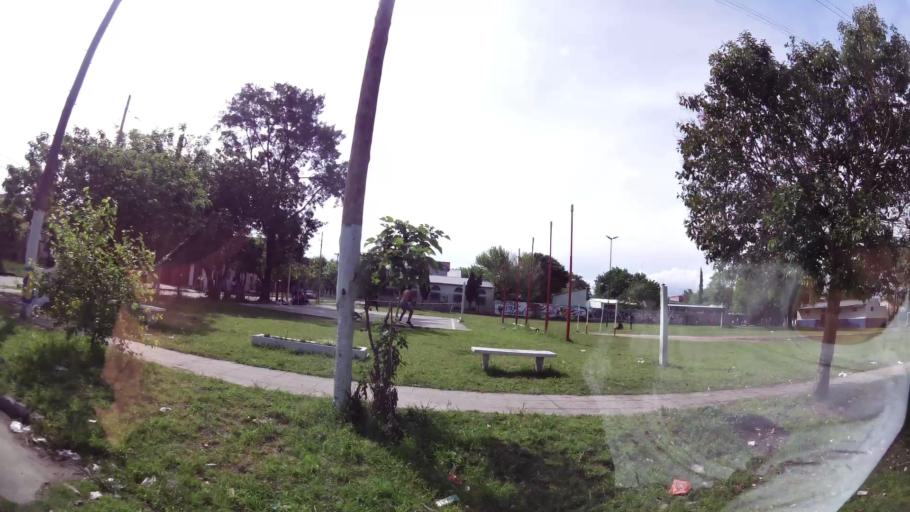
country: AR
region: Buenos Aires
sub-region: Partido de Quilmes
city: Quilmes
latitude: -34.7626
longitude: -58.2375
